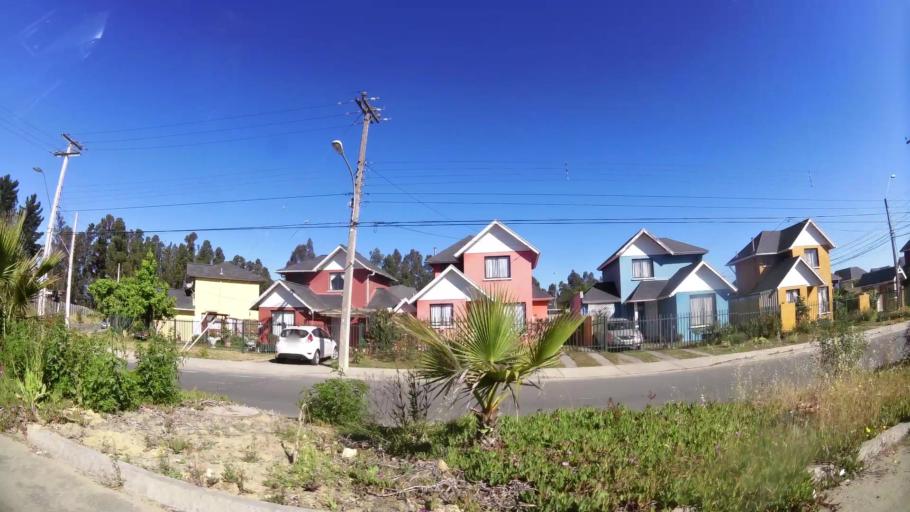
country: CL
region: Valparaiso
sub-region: Provincia de Valparaiso
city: Vina del Mar
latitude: -33.1265
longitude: -71.5634
